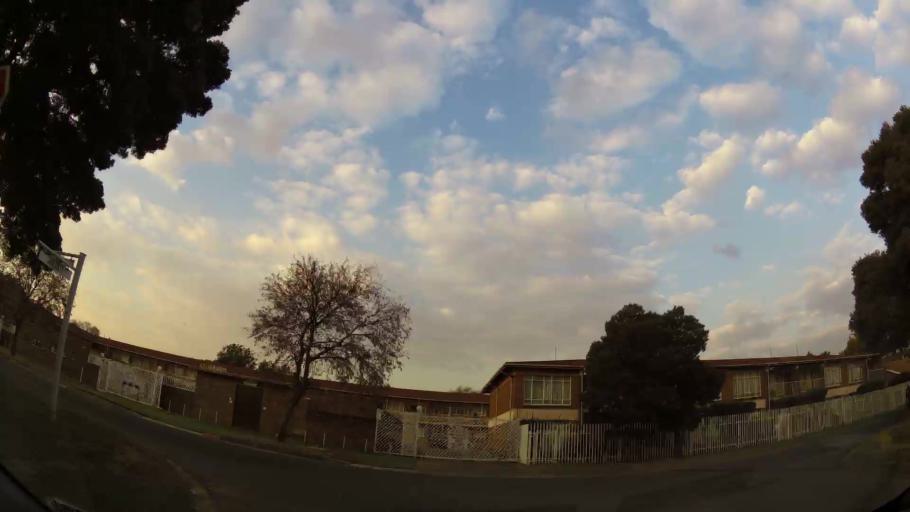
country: ZA
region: Gauteng
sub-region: Ekurhuleni Metropolitan Municipality
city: Benoni
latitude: -26.1636
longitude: 28.3056
